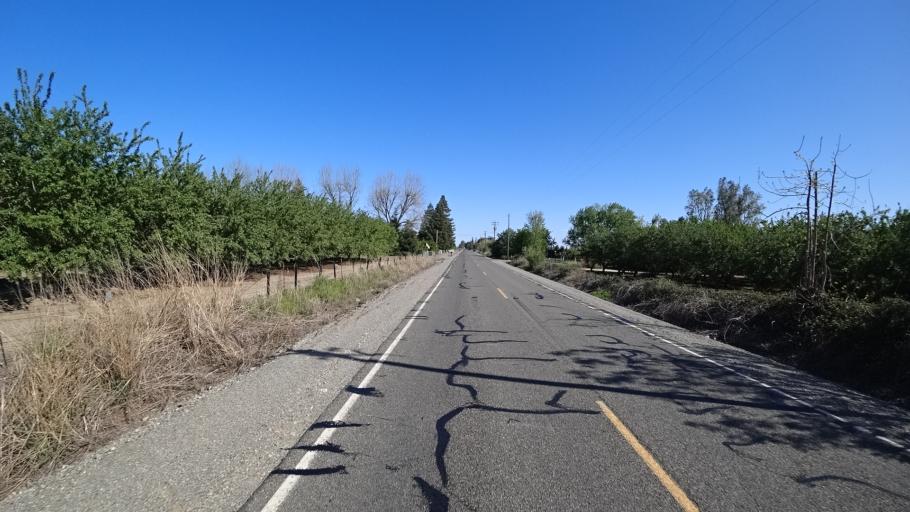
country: US
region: California
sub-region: Glenn County
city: Orland
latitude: 39.7391
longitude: -122.1410
